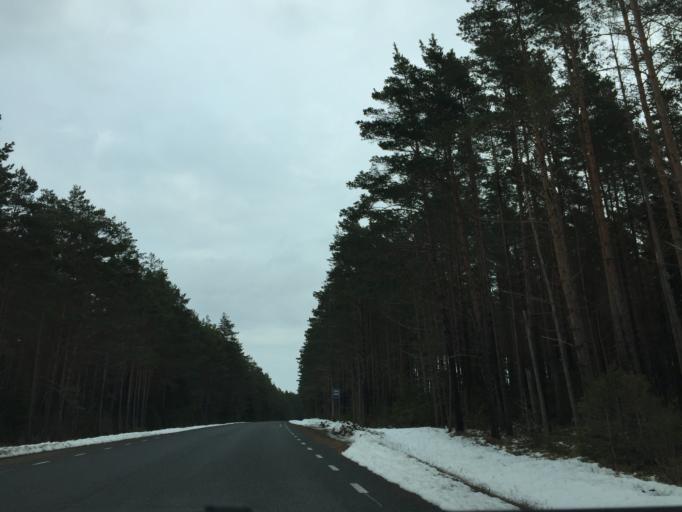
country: EE
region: Saare
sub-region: Kuressaare linn
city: Kuressaare
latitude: 58.4267
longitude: 22.1827
